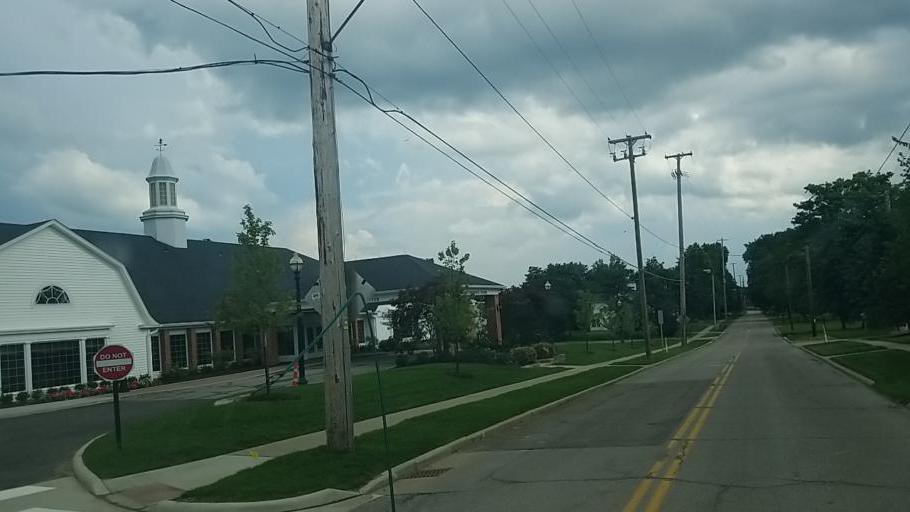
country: US
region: Ohio
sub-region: Medina County
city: Westfield Center
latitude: 41.0253
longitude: -81.9335
